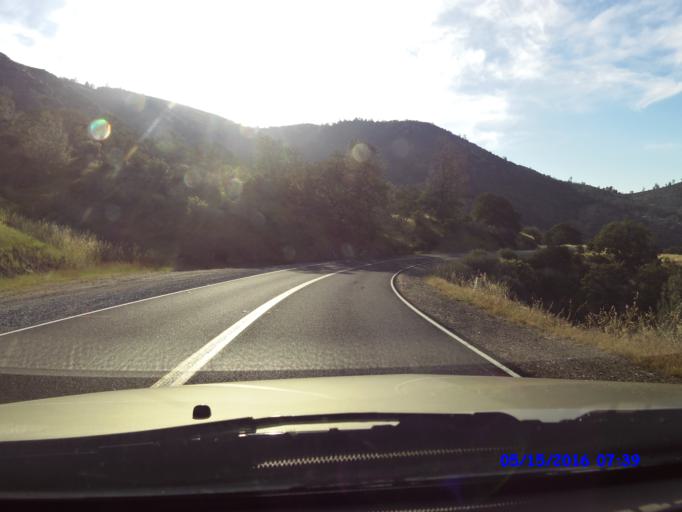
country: US
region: California
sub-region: Mariposa County
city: Mariposa
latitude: 37.6639
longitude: -120.1552
